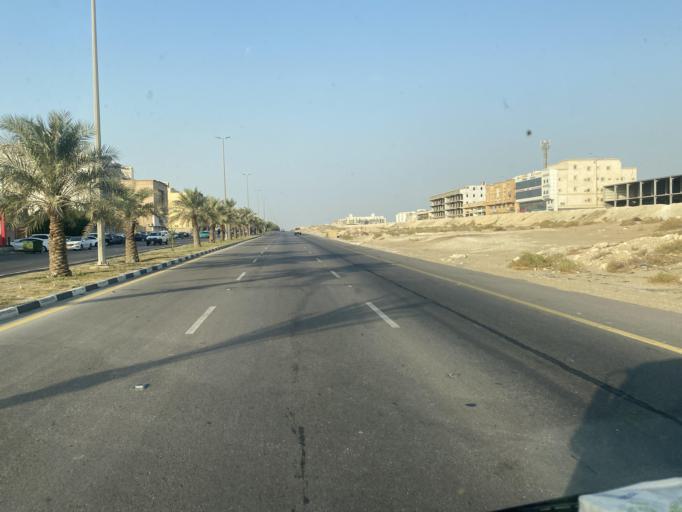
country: SA
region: Eastern Province
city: Dhahran
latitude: 26.3563
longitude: 50.0606
